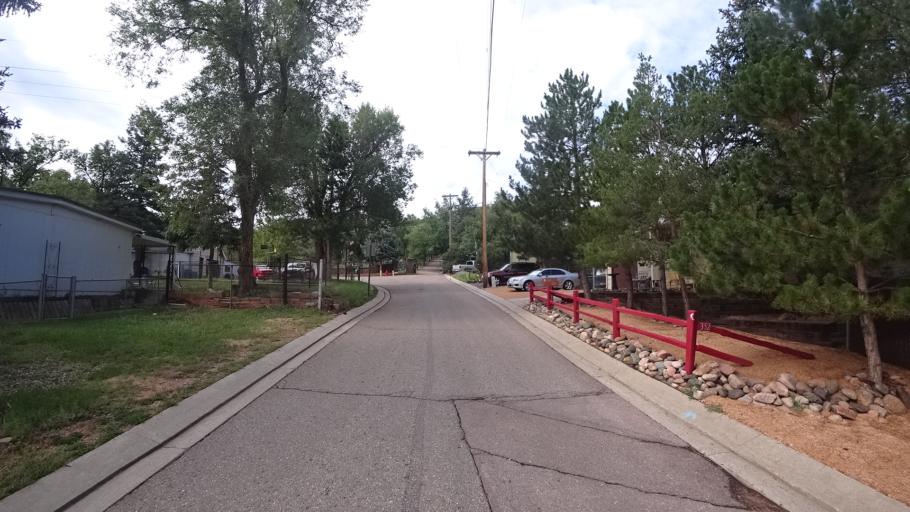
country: US
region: Colorado
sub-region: El Paso County
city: Manitou Springs
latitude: 38.8539
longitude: -104.9026
